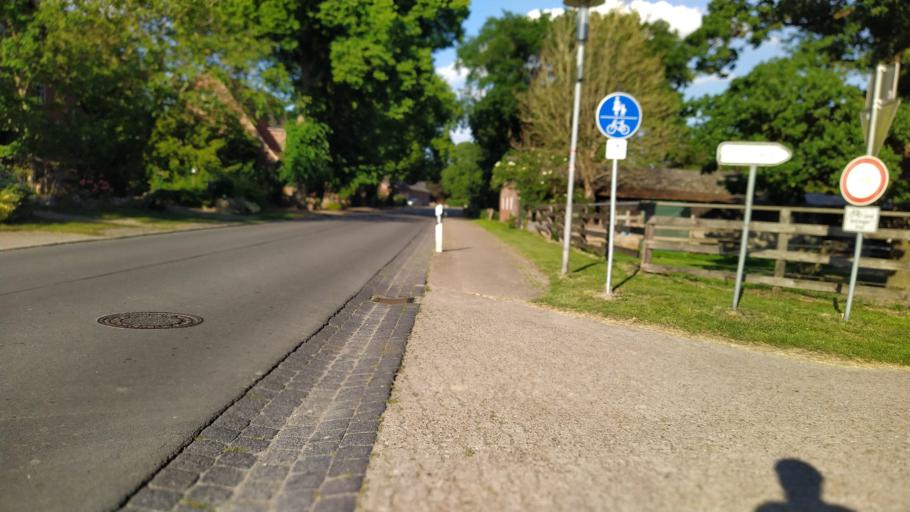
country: DE
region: Lower Saxony
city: Lintig
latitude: 53.5968
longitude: 8.9288
